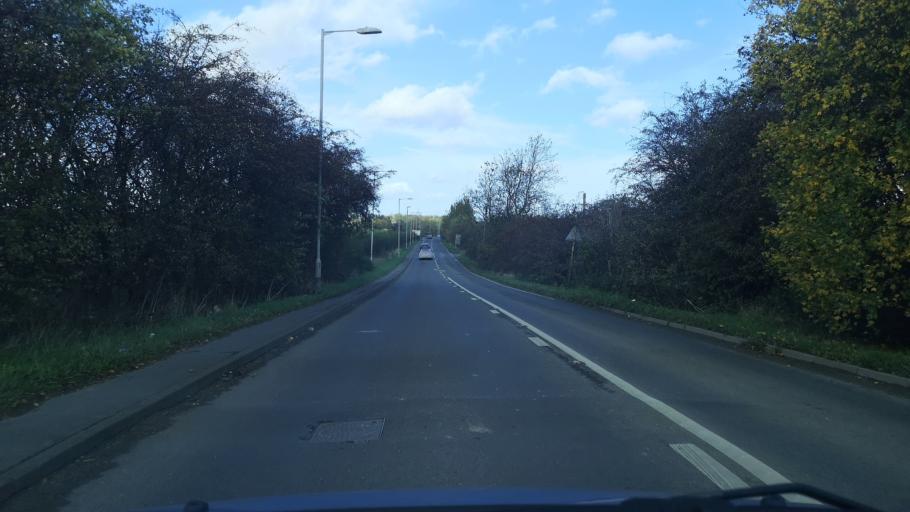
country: GB
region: England
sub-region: City and Borough of Wakefield
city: Featherstone
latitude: 53.6777
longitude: -1.3779
